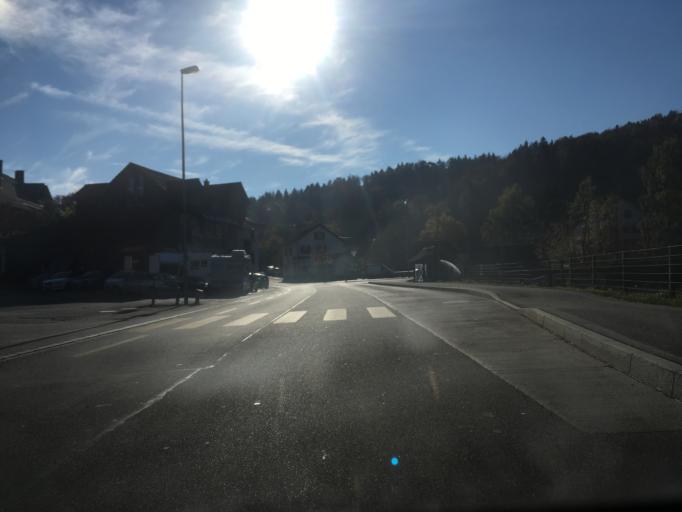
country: CH
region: Zurich
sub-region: Bezirk Affoltern
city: Affoltern / Sonnenberg
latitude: 47.2848
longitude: 8.4863
